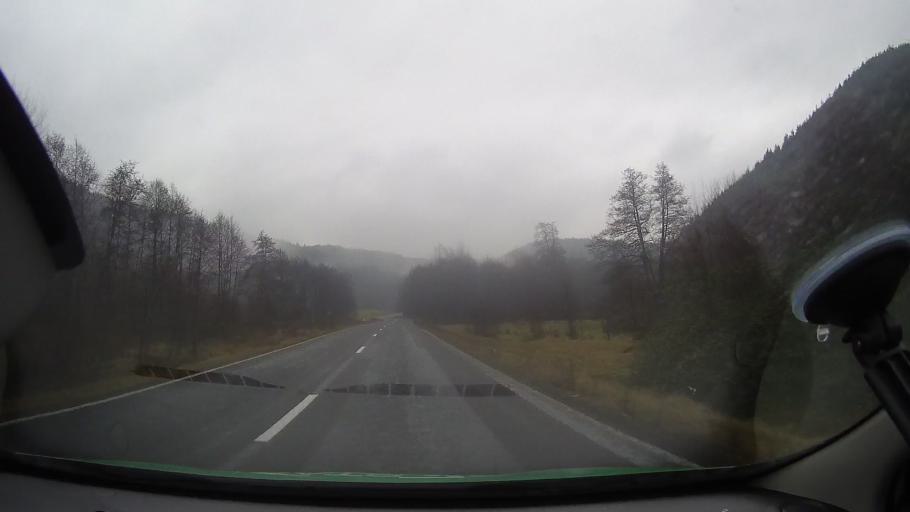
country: RO
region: Arad
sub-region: Comuna Plescuta
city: Plescuta
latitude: 46.3129
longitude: 22.4564
